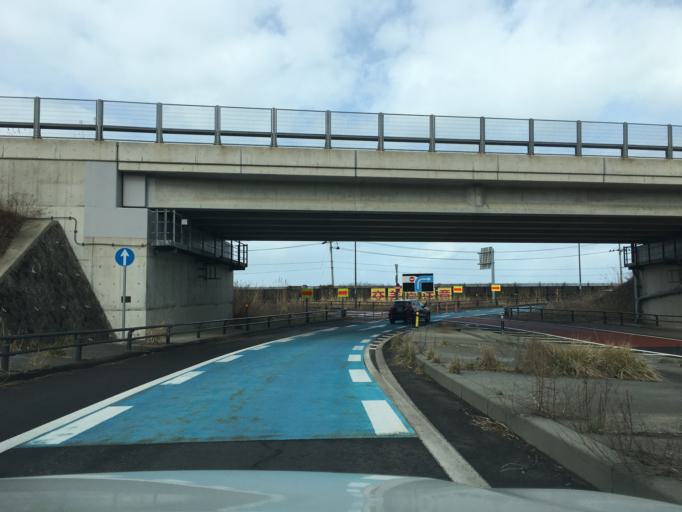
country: JP
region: Yamagata
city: Yuza
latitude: 39.2949
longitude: 139.9768
